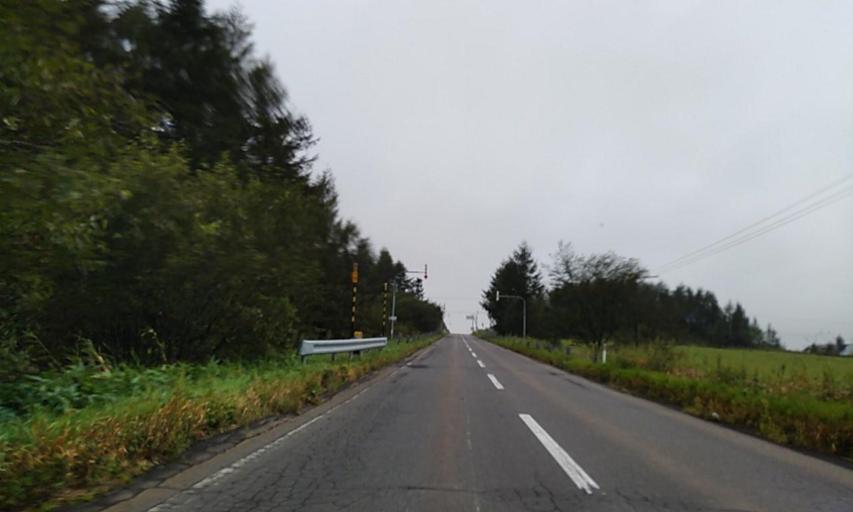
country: JP
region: Hokkaido
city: Shibetsu
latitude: 43.5075
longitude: 144.6656
